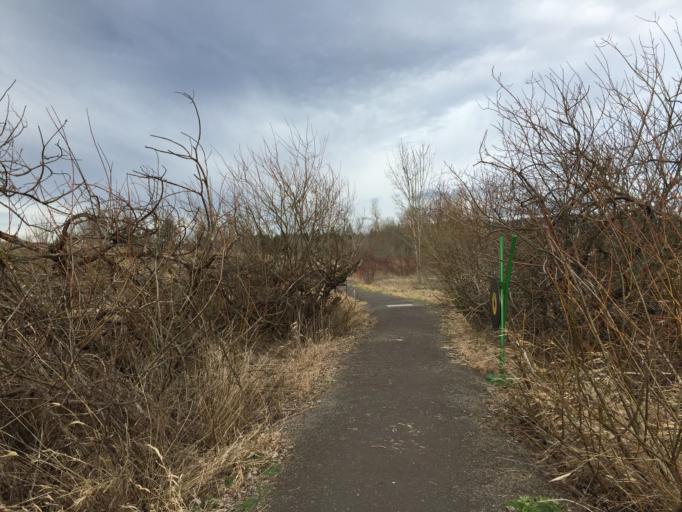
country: US
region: Washington
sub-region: Clark County
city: Washougal
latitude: 45.5694
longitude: -122.3156
